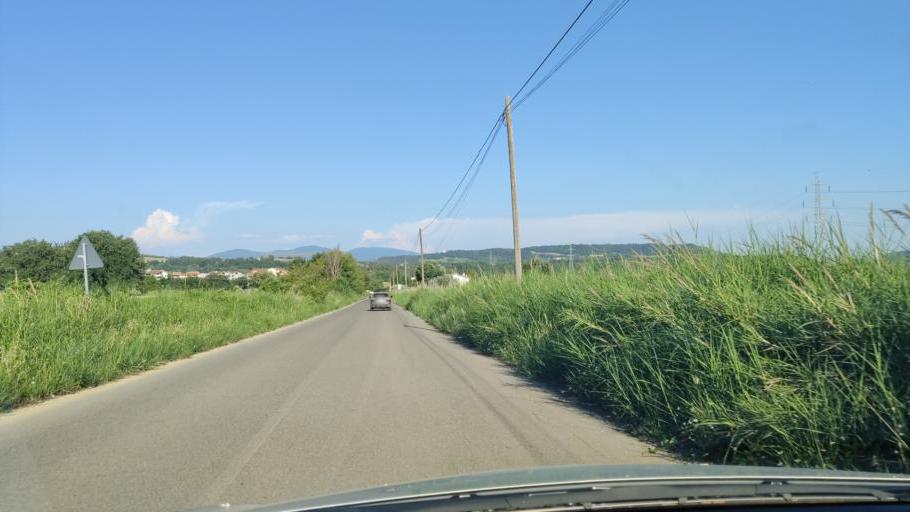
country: IT
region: Latium
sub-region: Provincia di Viterbo
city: Orte
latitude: 42.4695
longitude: 12.3841
